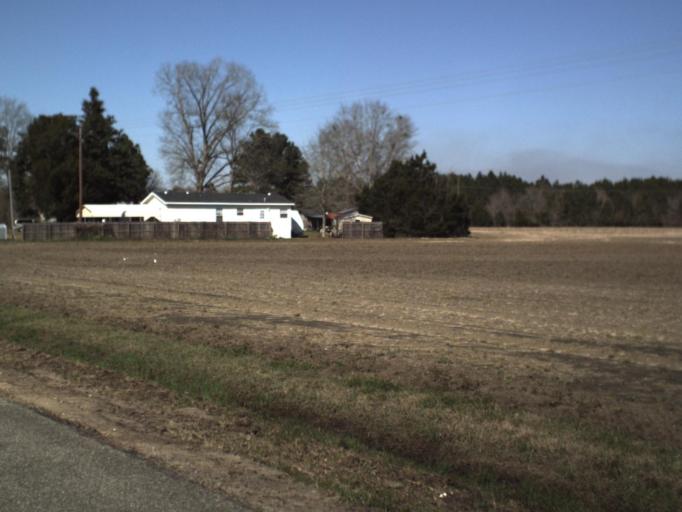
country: US
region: Florida
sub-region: Calhoun County
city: Blountstown
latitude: 30.4919
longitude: -85.1102
